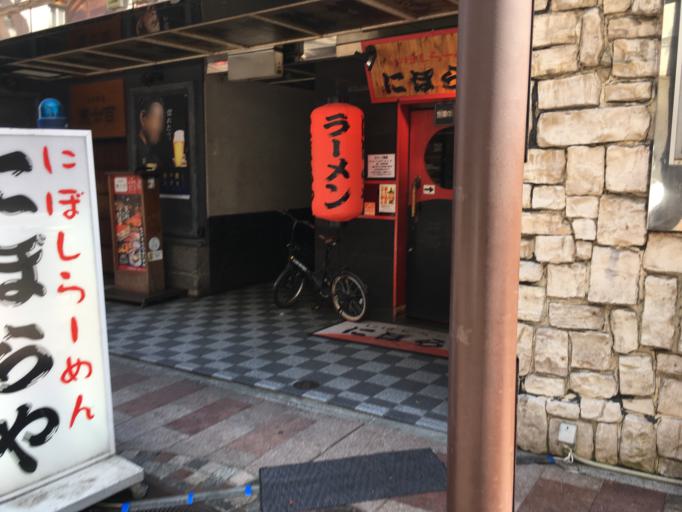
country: JP
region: Kumamoto
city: Kumamoto
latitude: 32.8000
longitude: 130.7062
